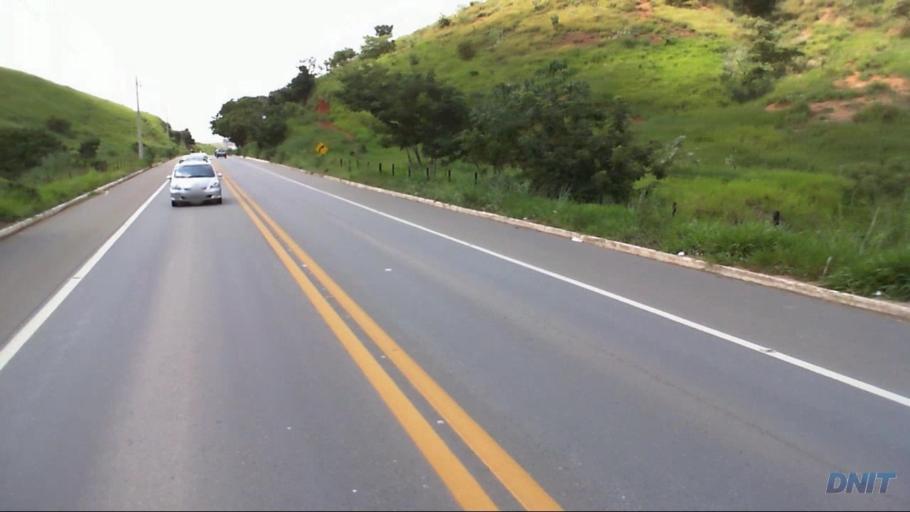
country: BR
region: Minas Gerais
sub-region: Governador Valadares
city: Governador Valadares
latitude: -18.8452
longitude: -41.9751
